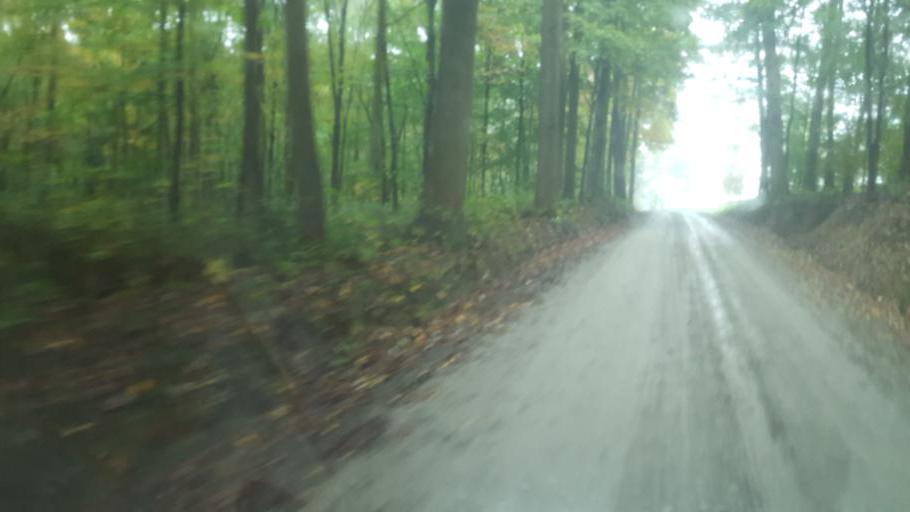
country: US
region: Ohio
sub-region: Tuscarawas County
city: Sugarcreek
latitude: 40.5900
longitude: -81.7489
